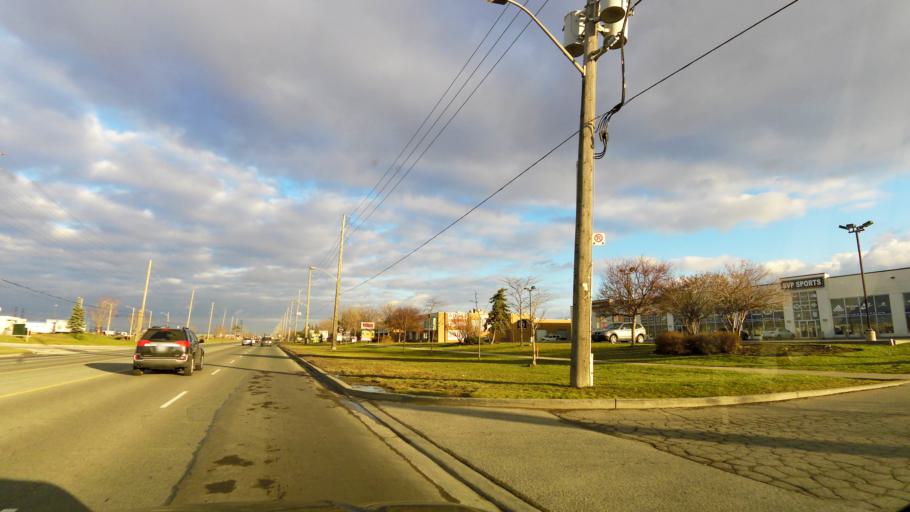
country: CA
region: Ontario
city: Etobicoke
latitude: 43.7532
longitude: -79.6240
